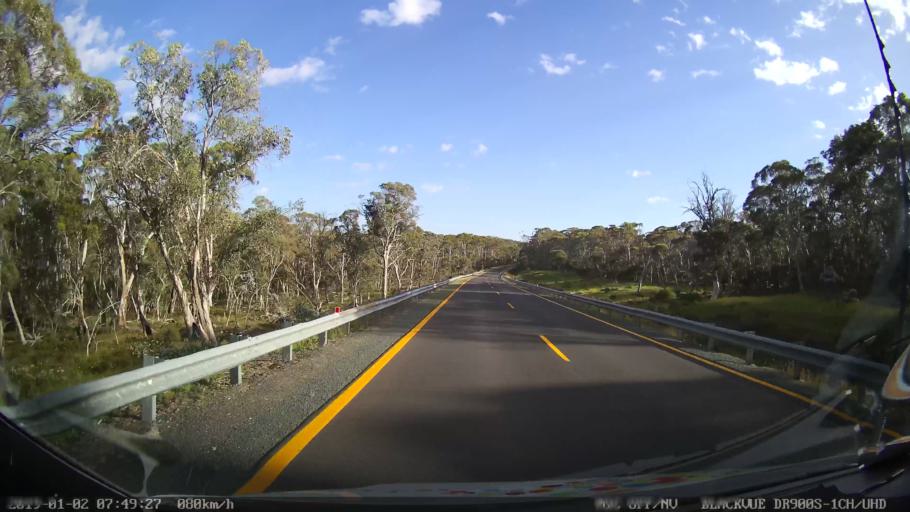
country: AU
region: New South Wales
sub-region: Tumut Shire
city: Tumut
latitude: -35.7416
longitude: 148.5224
